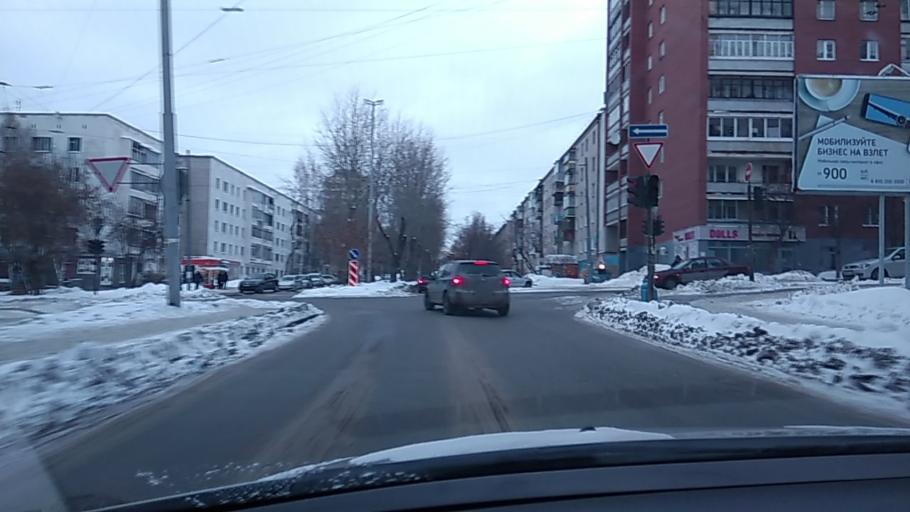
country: RU
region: Sverdlovsk
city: Yekaterinburg
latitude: 56.8230
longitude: 60.6360
